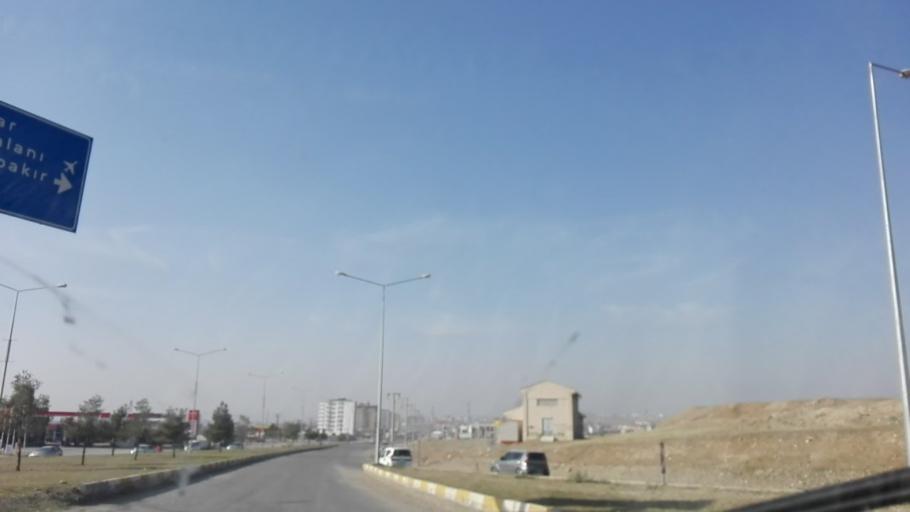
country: TR
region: Batman
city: Aydinkonak
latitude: 37.8745
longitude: 41.1744
